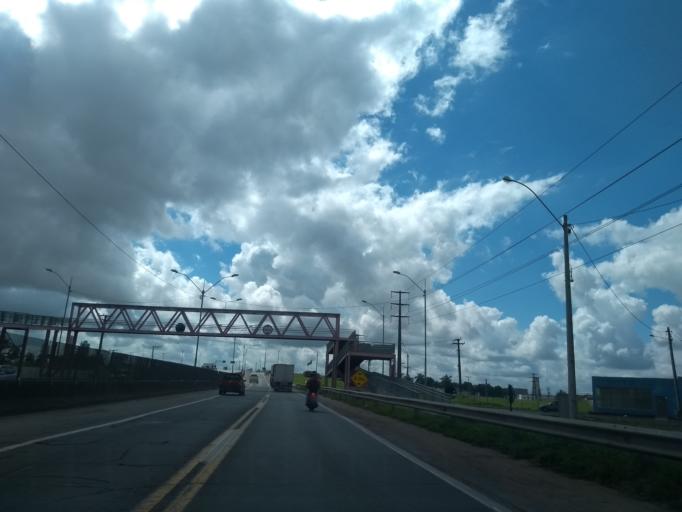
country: BR
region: Bahia
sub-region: Feira De Santana
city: Feira de Santana
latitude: -12.2749
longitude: -38.9375
